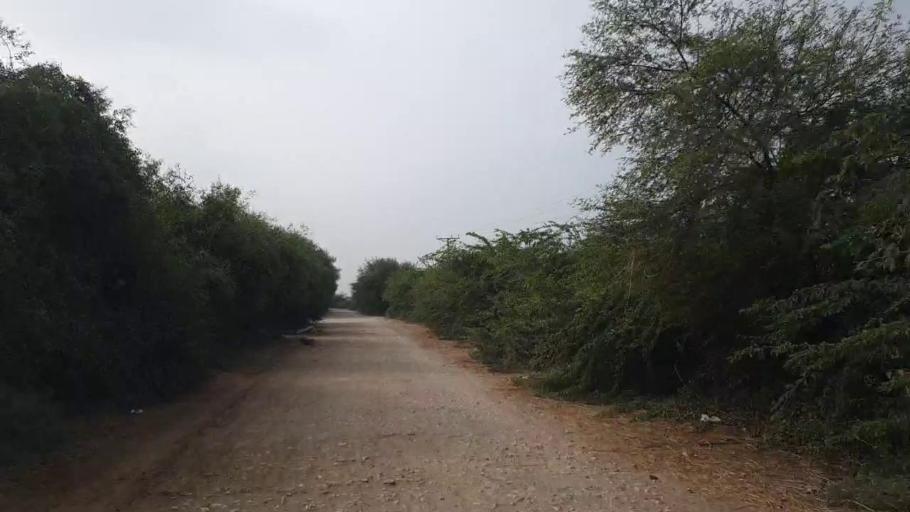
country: PK
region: Sindh
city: Matli
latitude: 24.9584
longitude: 68.5831
